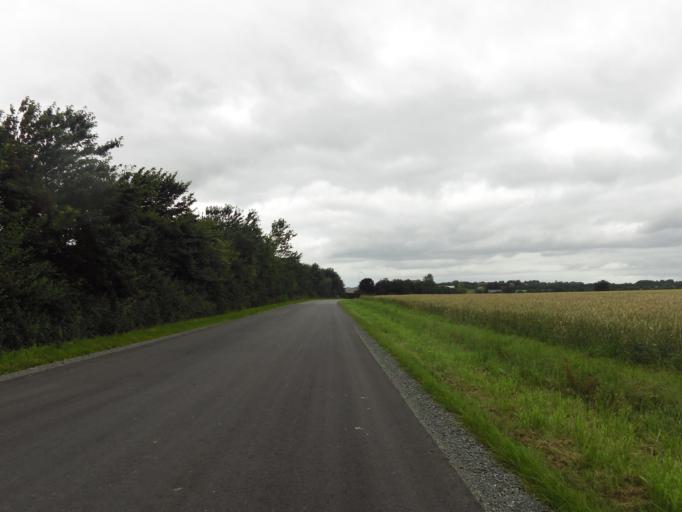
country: DK
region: South Denmark
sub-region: Haderslev Kommune
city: Gram
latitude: 55.2598
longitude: 9.1608
